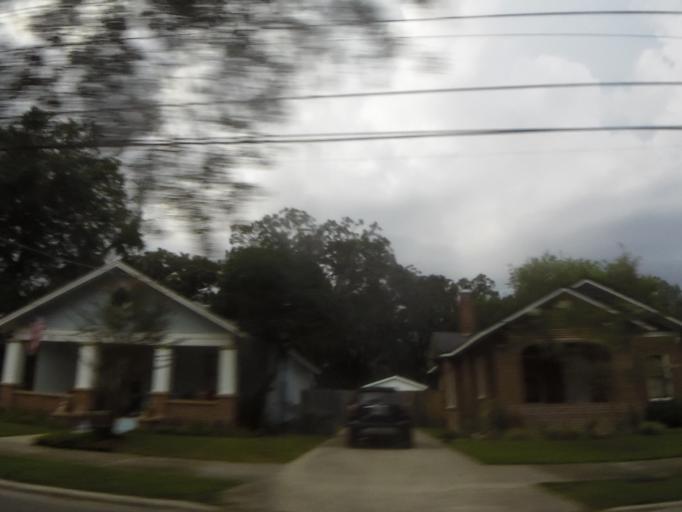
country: US
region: Florida
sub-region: Duval County
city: Jacksonville
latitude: 30.2936
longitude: -81.7119
